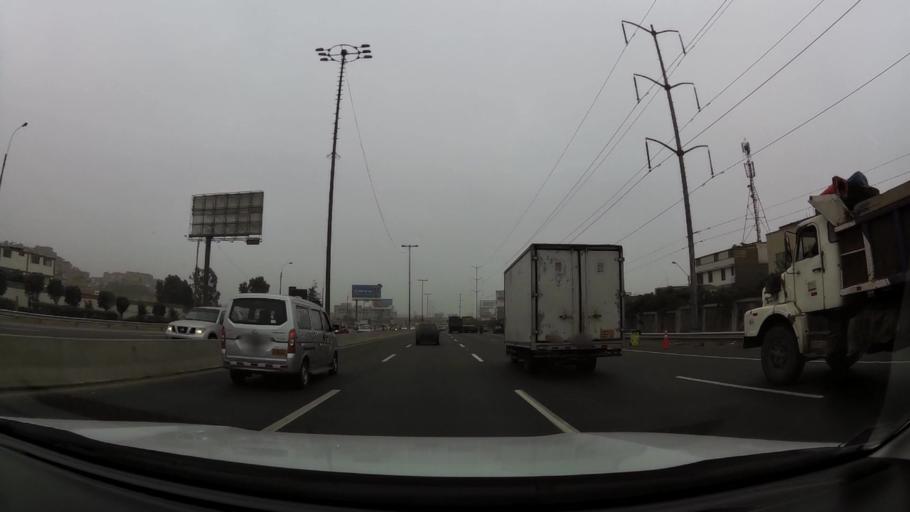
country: PE
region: Lima
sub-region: Lima
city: Surco
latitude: -12.1422
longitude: -76.9814
